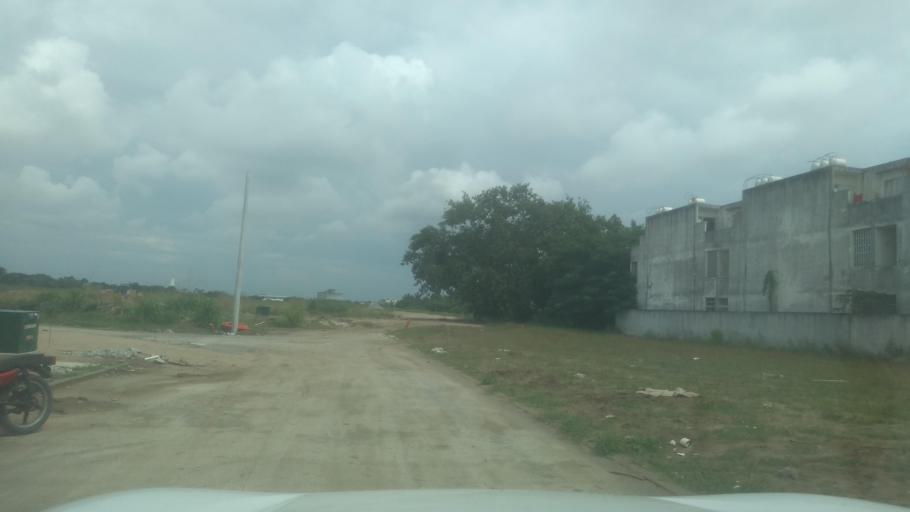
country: MX
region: Veracruz
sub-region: Medellin
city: Fraccionamiento Arboledas San Ramon
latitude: 19.0931
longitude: -96.1666
